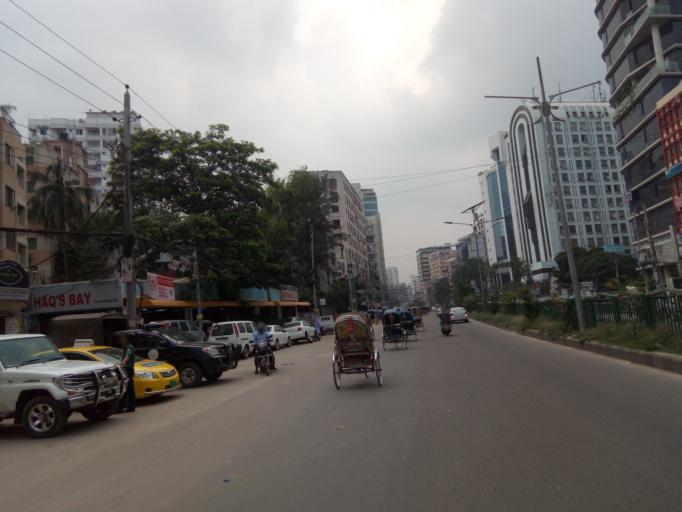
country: BD
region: Dhaka
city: Paltan
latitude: 23.7365
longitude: 90.4133
